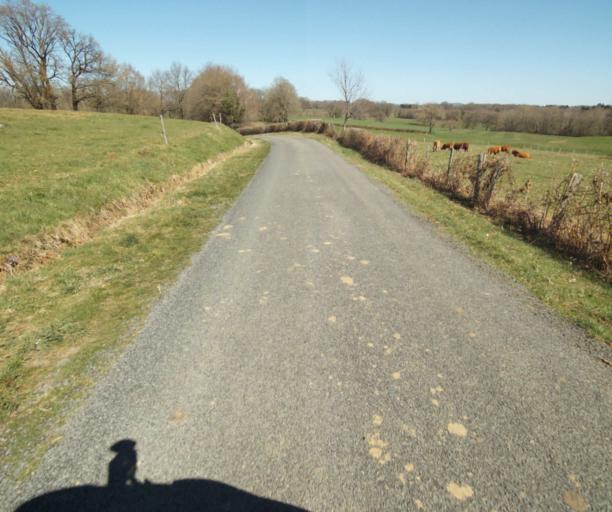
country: FR
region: Limousin
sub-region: Departement de la Correze
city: Seilhac
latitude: 45.3861
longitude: 1.6814
